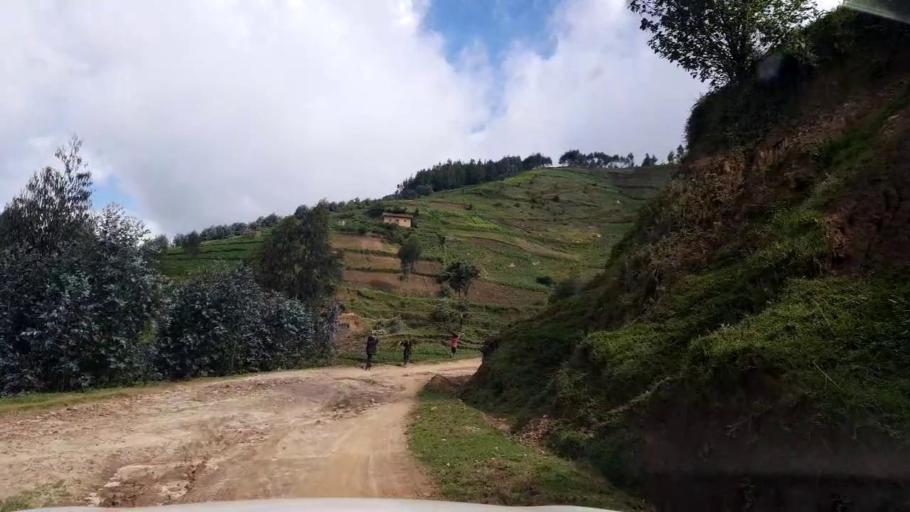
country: RW
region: Western Province
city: Kibuye
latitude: -1.8802
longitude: 29.4753
